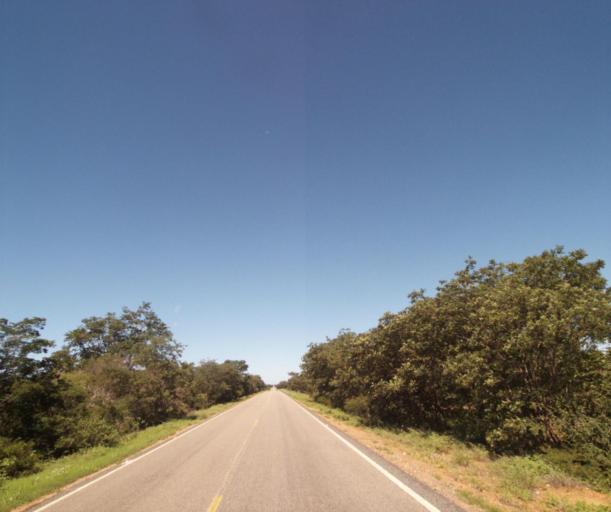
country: BR
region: Bahia
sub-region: Palmas De Monte Alto
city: Palmas de Monte Alto
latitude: -14.2587
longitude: -43.2757
